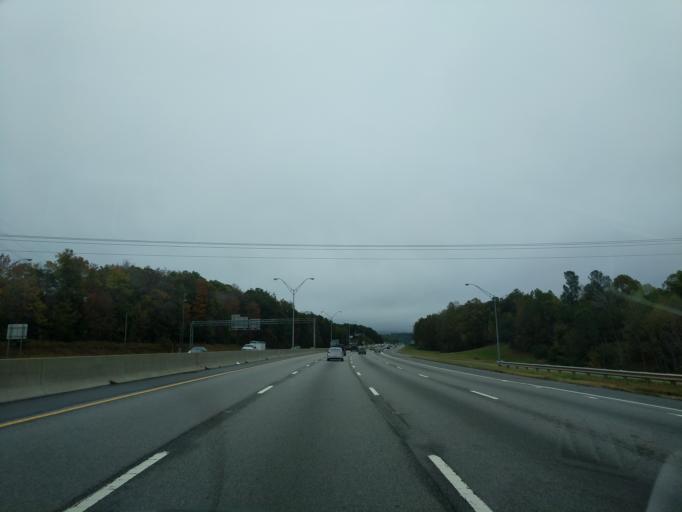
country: US
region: North Carolina
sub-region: Orange County
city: Hillsborough
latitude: 36.0726
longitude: -79.1596
